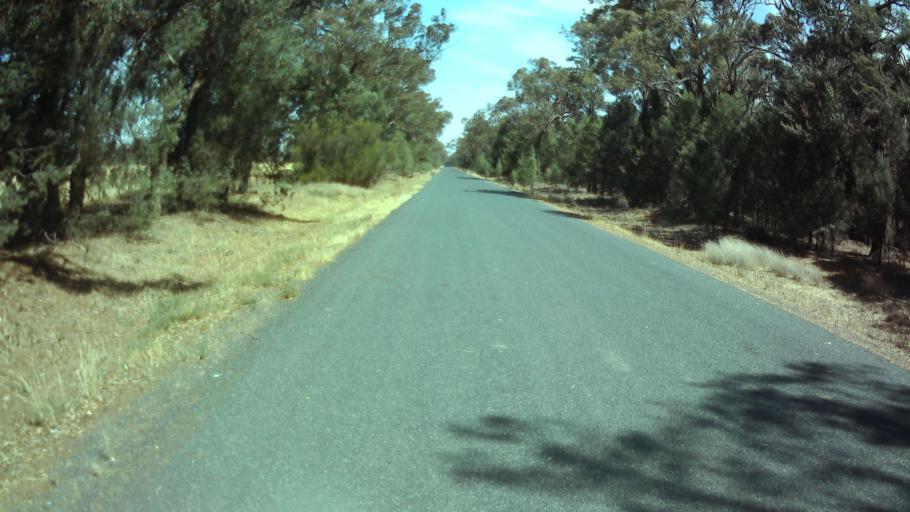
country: AU
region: New South Wales
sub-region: Weddin
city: Grenfell
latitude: -34.0591
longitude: 148.1318
